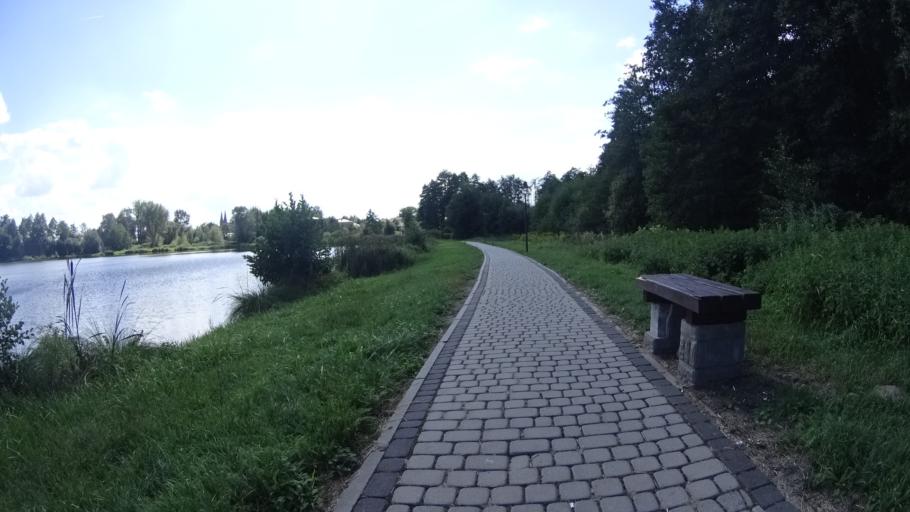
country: PL
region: Masovian Voivodeship
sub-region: Powiat grojecki
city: Mogielnica
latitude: 51.6986
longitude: 20.7233
